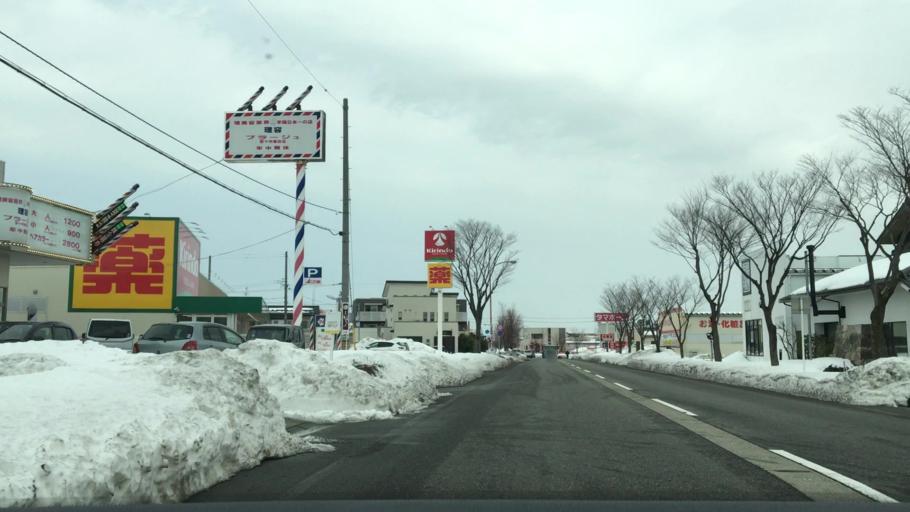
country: JP
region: Ishikawa
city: Nonoichi
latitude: 36.5092
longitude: 136.6081
